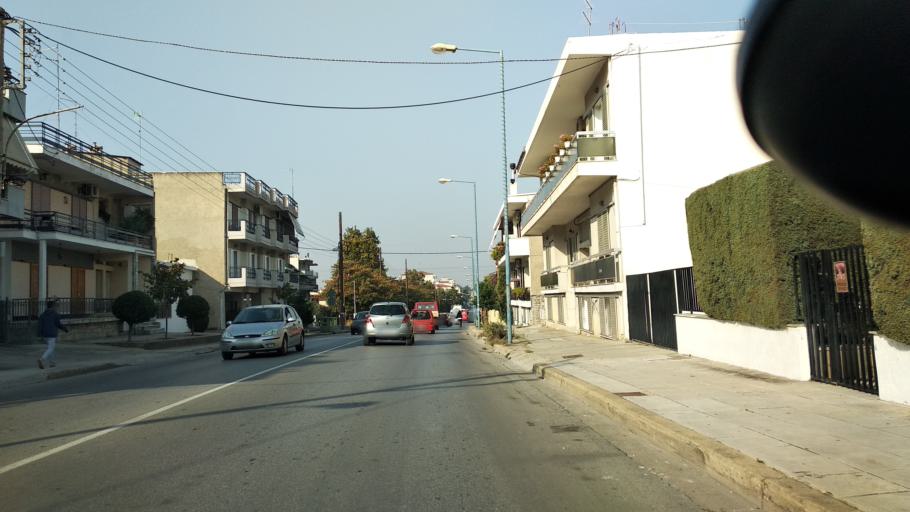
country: GR
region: Thessaly
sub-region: Nomos Larisis
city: Larisa
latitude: 39.6325
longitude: 22.3953
